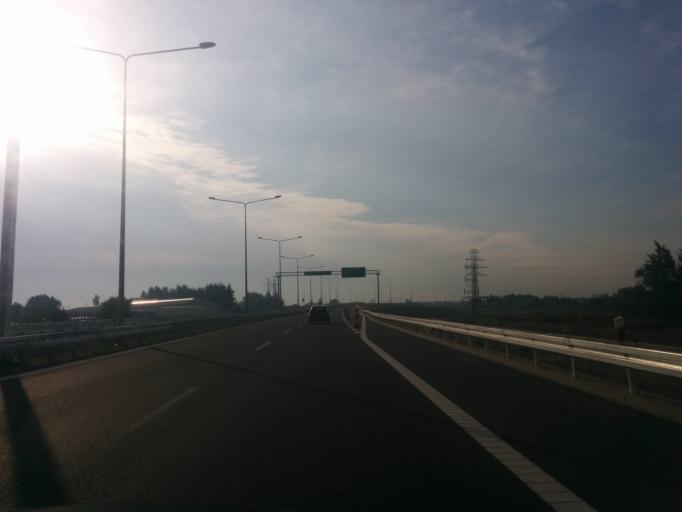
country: PL
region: Masovian Voivodeship
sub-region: Powiat pruszkowski
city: Nowe Grocholice
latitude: 52.1181
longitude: 20.8853
